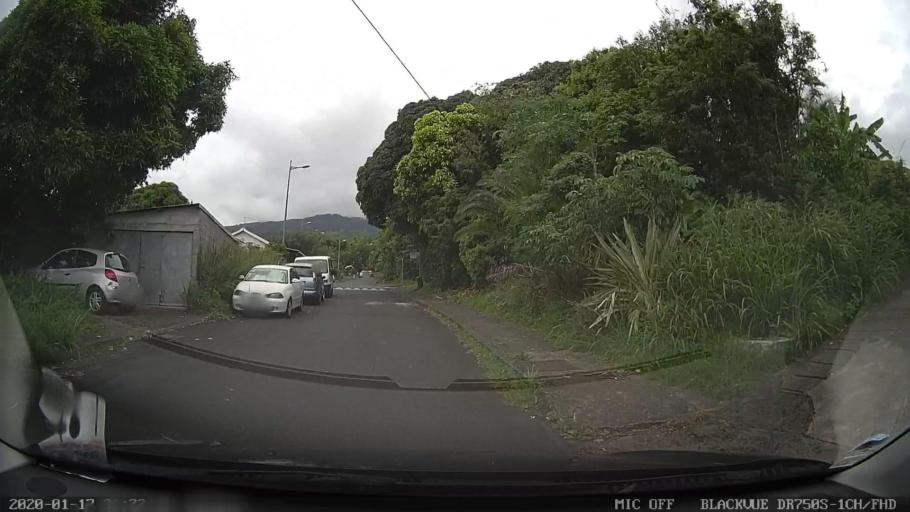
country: RE
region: Reunion
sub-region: Reunion
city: Saint-Denis
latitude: -20.9178
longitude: 55.4870
